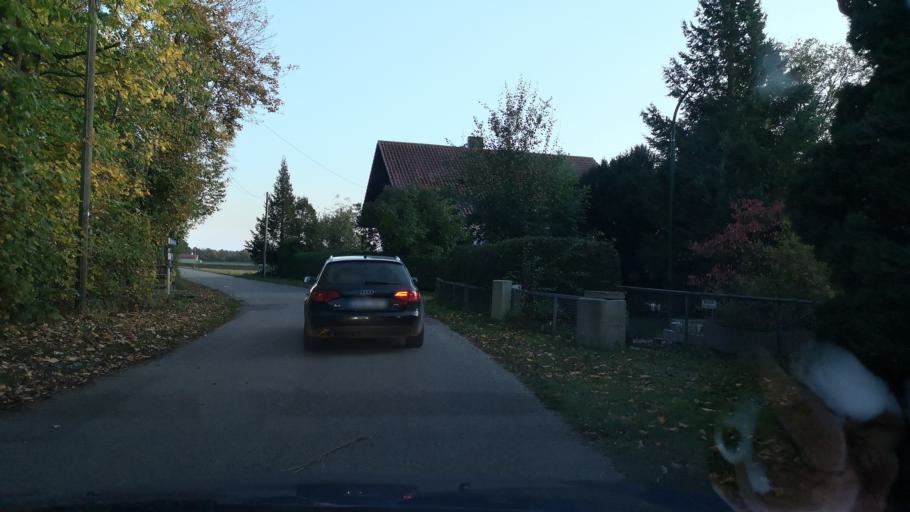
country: DE
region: Bavaria
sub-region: Upper Bavaria
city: Eichenried
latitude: 48.2320
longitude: 11.7557
